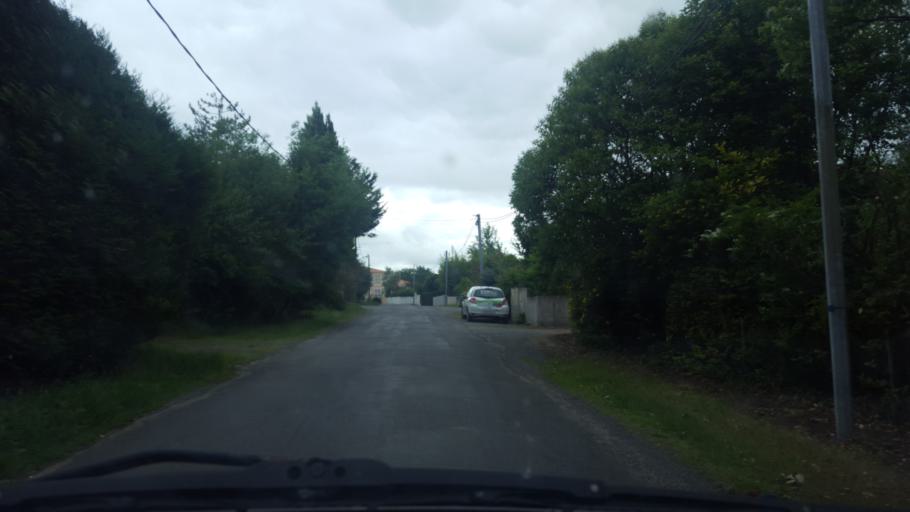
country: FR
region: Pays de la Loire
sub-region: Departement de la Loire-Atlantique
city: Saint-Philbert-de-Grand-Lieu
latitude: 47.0282
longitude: -1.6494
